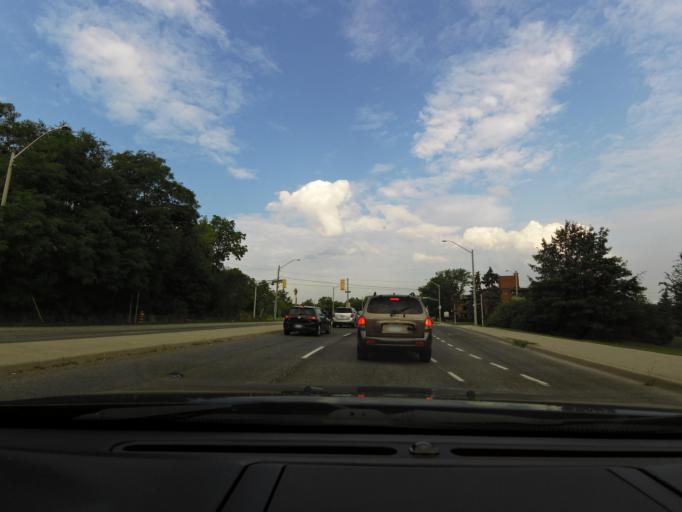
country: CA
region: Ontario
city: Hamilton
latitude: 43.2209
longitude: -79.7768
